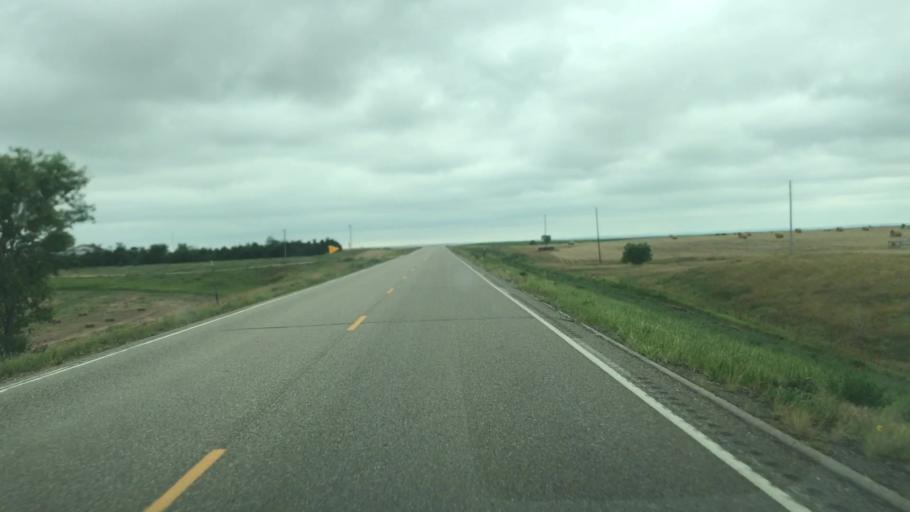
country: US
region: South Dakota
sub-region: Jackson County
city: Kadoka
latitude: 43.8226
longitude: -101.5224
